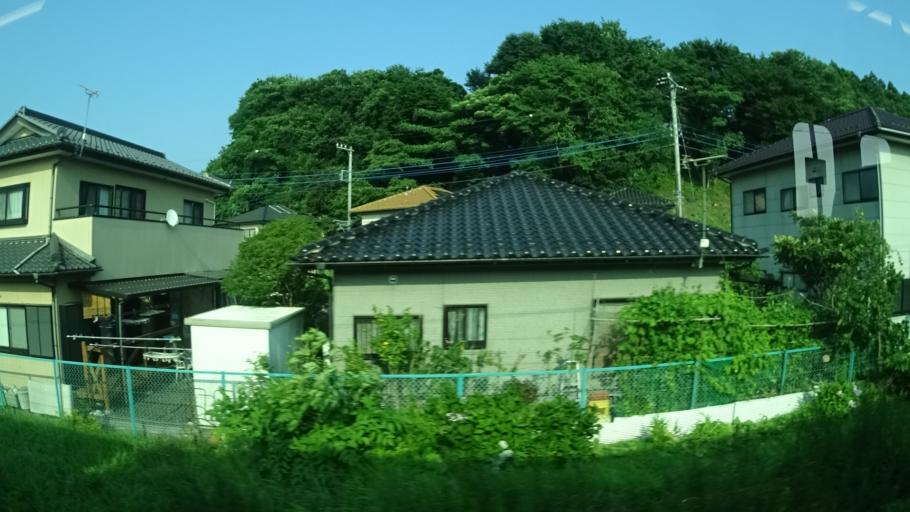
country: JP
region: Ibaraki
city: Kitaibaraki
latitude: 36.8537
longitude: 140.7792
